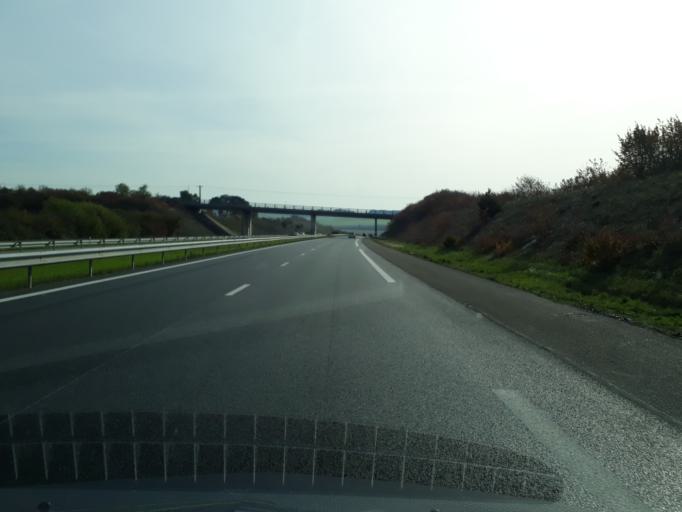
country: FR
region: Bourgogne
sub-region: Departement de l'Yonne
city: Sergines
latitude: 48.3264
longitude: 3.2246
